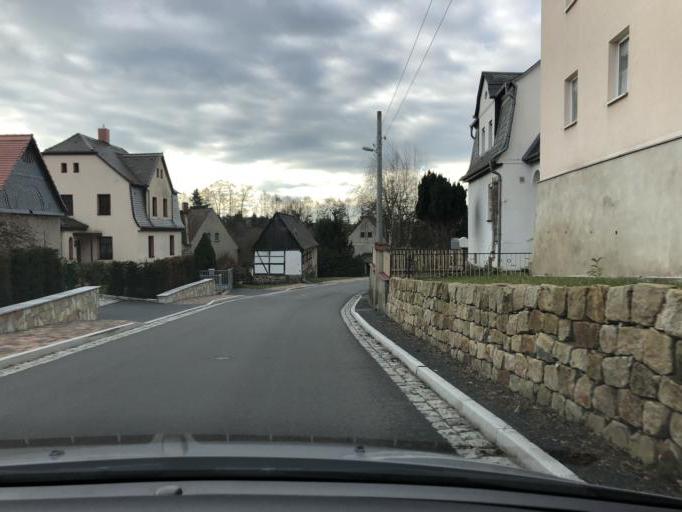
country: DE
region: Saxony
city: Grossbothen
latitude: 51.1894
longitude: 12.7864
